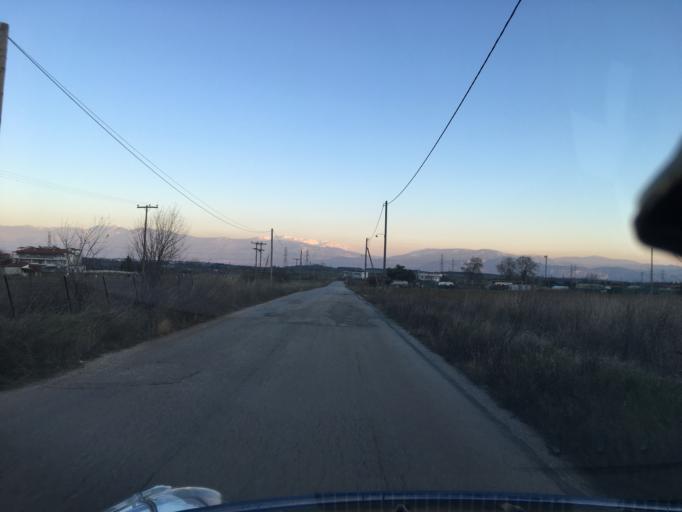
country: GR
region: West Macedonia
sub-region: Nomos Kozanis
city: Kozani
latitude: 40.2580
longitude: 21.7545
